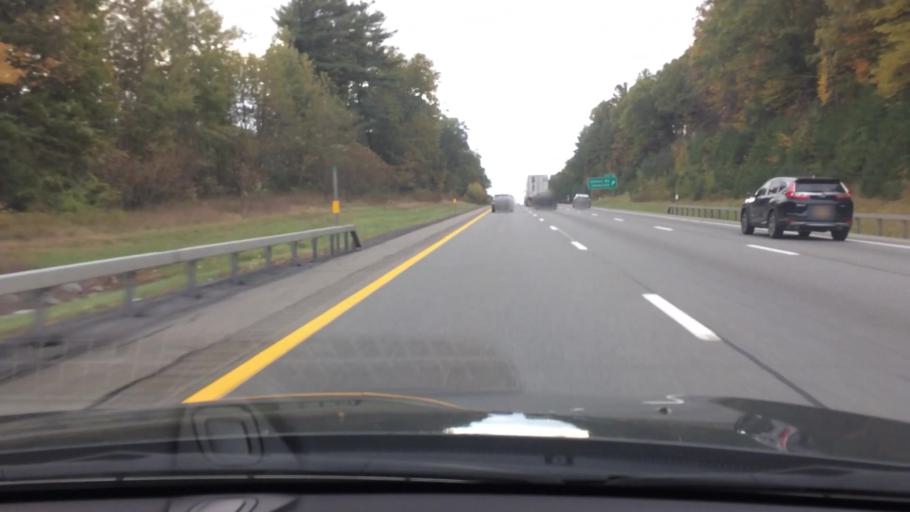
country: US
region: New York
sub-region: Saratoga County
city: Country Knolls
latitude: 42.9081
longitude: -73.7911
